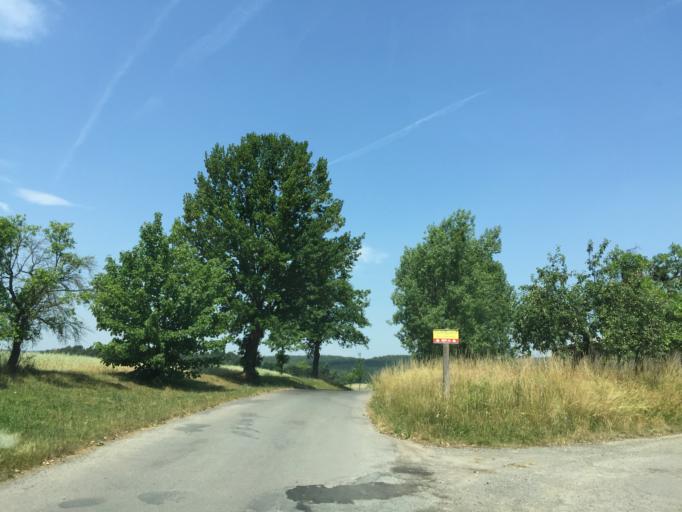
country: DE
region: Thuringia
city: Rudolstadt
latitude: 50.7507
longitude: 11.3458
